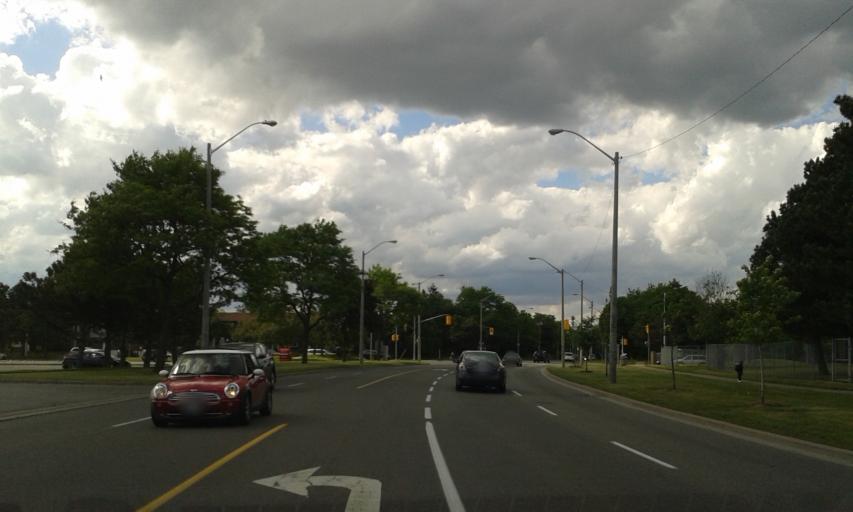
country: CA
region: Ontario
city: Scarborough
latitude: 43.8105
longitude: -79.2682
